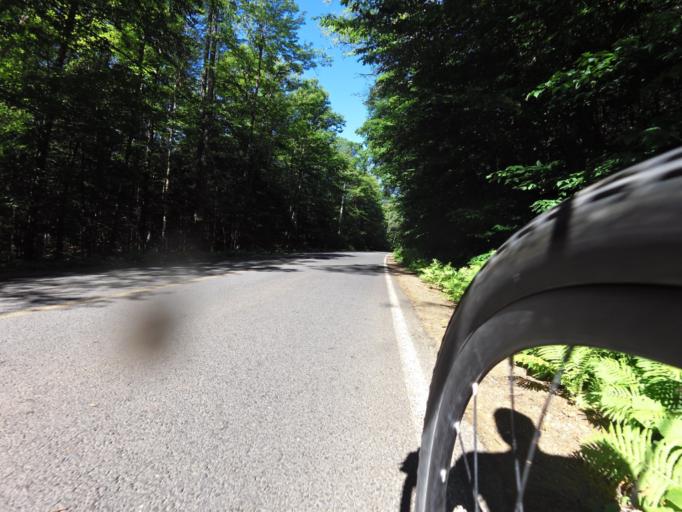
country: CA
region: Quebec
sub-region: Laurentides
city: Brownsburg-Chatham
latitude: 45.8860
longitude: -74.5817
